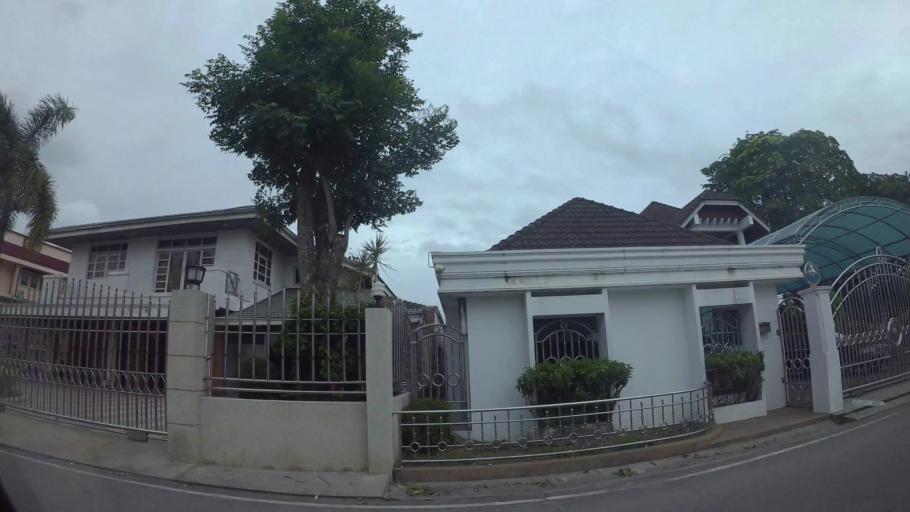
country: TH
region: Rayong
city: Rayong
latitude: 12.6603
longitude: 101.2751
